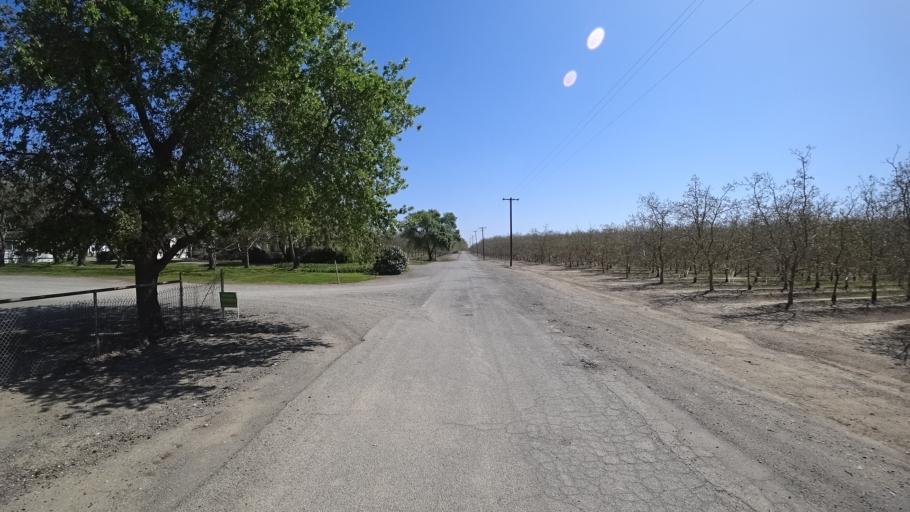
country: US
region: California
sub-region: Glenn County
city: Willows
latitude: 39.4990
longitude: -122.0275
